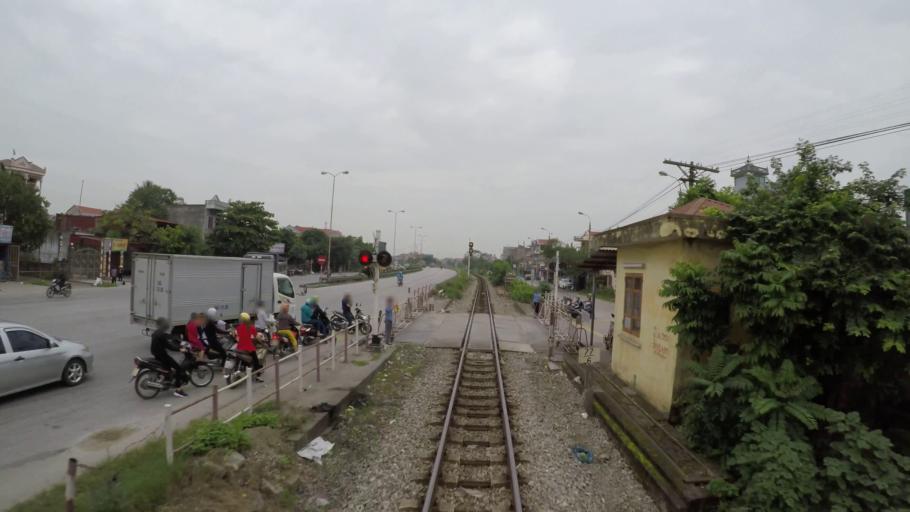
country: VN
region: Hai Duong
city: Phu Thai
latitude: 20.9722
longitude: 106.4749
